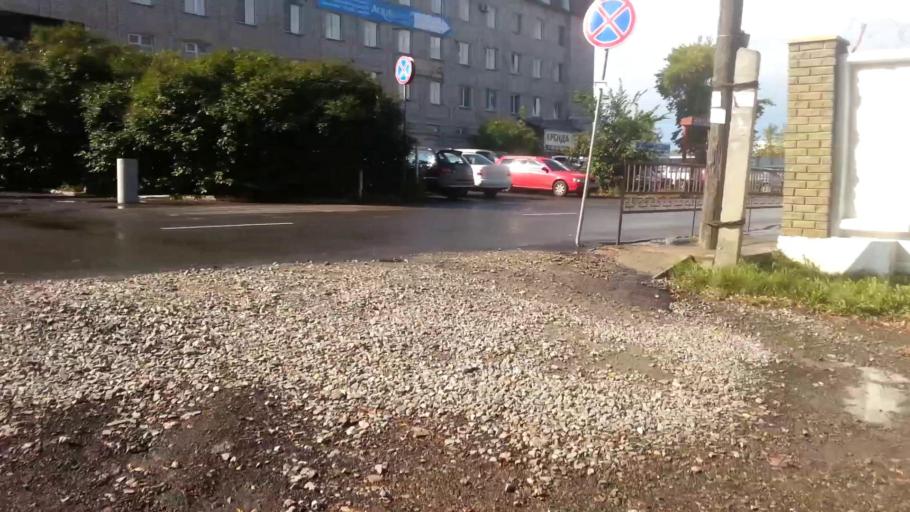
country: RU
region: Altai Krai
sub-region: Gorod Barnaulskiy
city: Barnaul
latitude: 53.3417
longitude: 83.7229
